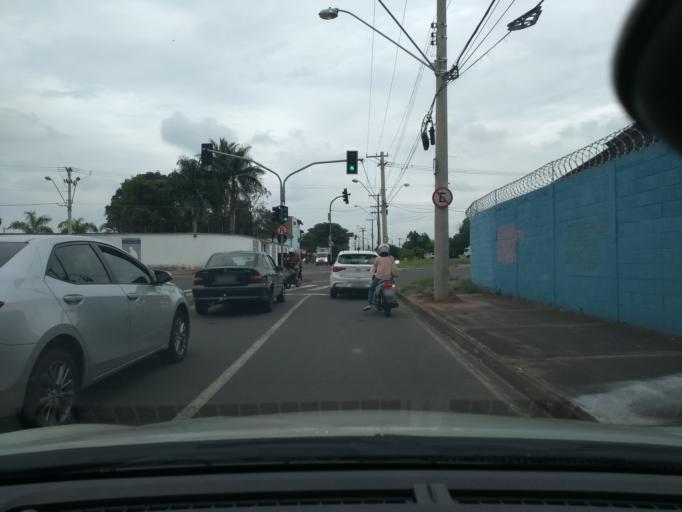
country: BR
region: Sao Paulo
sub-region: Rio Claro
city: Rio Claro
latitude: -22.3779
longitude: -47.5432
